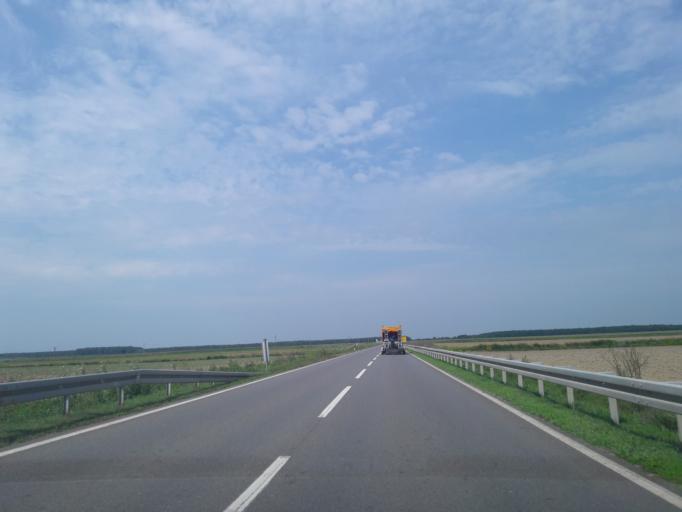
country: HR
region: Osjecko-Baranjska
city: Cepin
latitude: 45.5158
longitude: 18.5288
